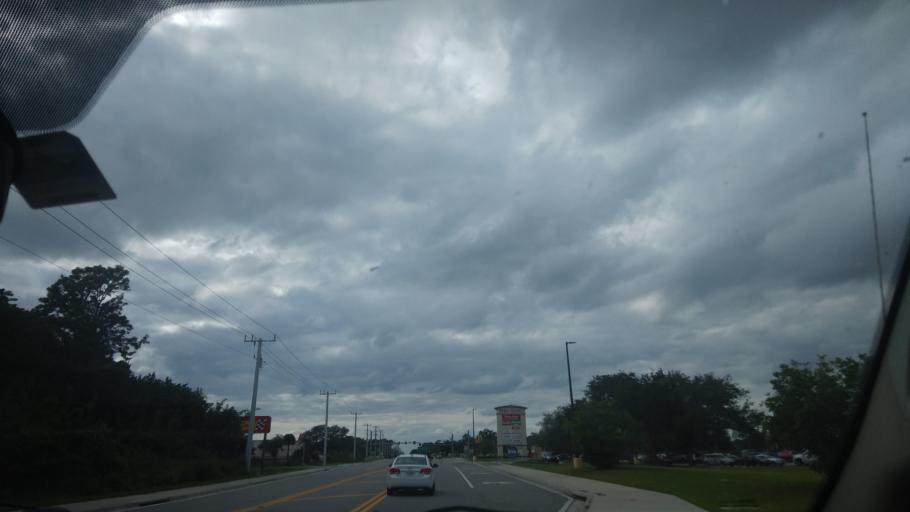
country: US
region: Florida
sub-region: Saint Lucie County
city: Lakewood Park
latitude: 27.5210
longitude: -80.3951
